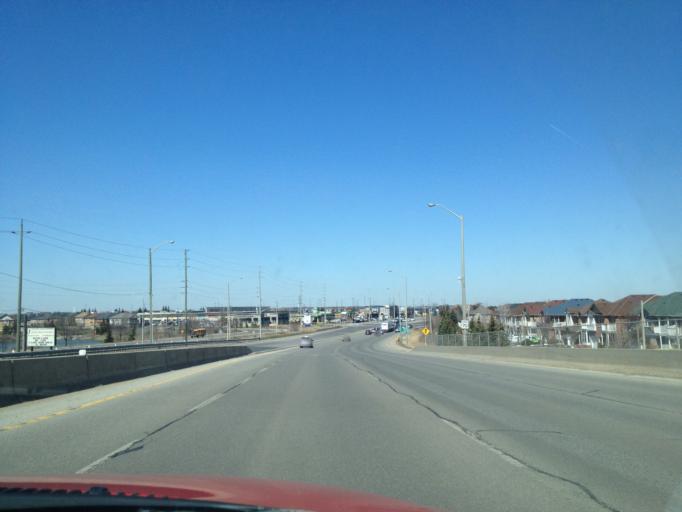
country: CA
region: Ontario
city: Brampton
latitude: 43.6777
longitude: -79.8163
